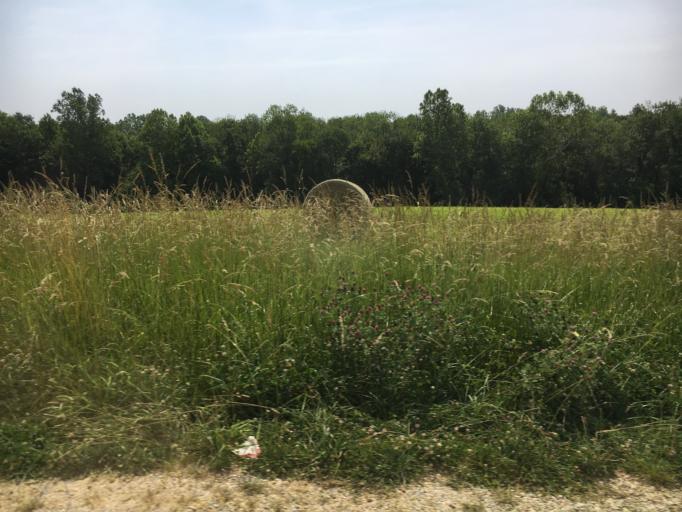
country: US
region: Virginia
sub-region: Goochland County
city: Goochland
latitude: 37.6902
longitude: -77.8326
